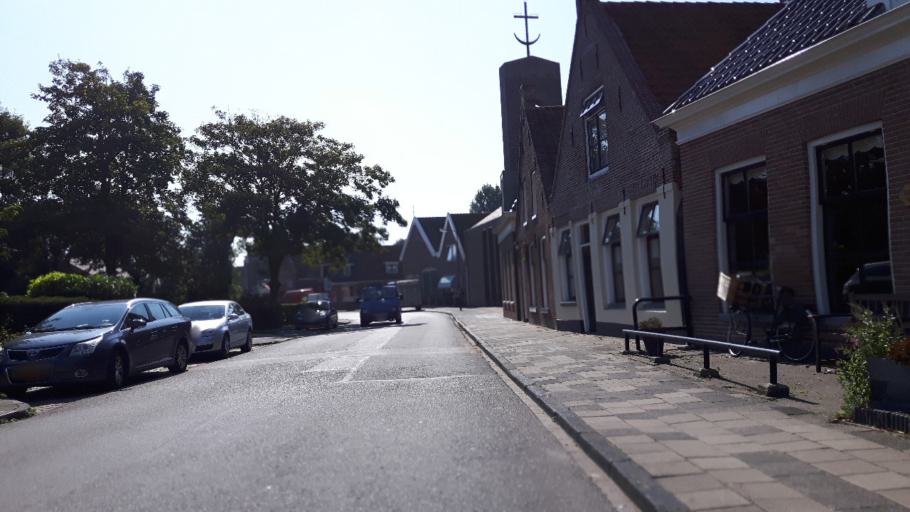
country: NL
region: Friesland
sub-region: Sudwest Fryslan
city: Makkum
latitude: 53.0580
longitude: 5.4019
